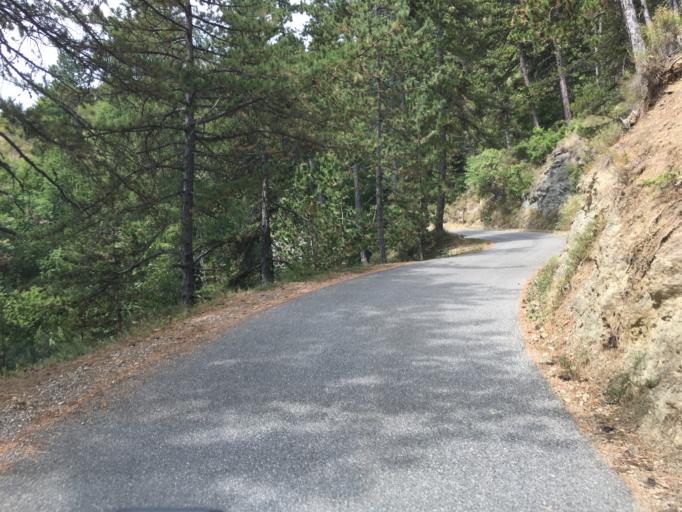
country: FR
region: Provence-Alpes-Cote d'Azur
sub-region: Departement des Alpes-de-Haute-Provence
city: Digne-les-Bains
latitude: 44.1989
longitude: 6.1423
